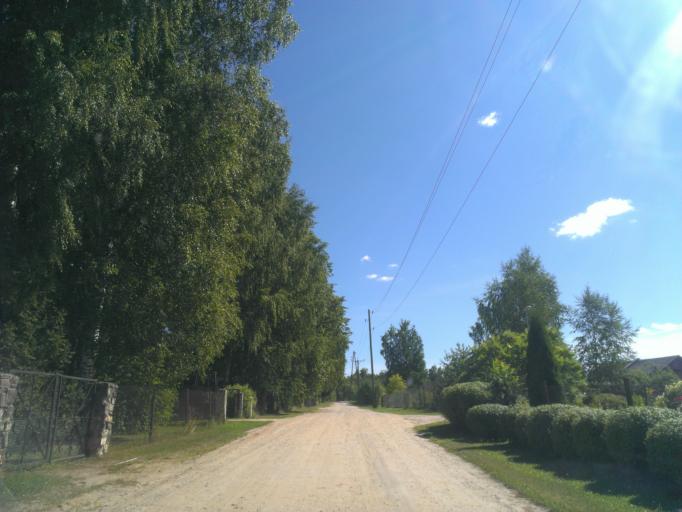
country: LV
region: Malpils
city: Malpils
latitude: 57.0112
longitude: 24.9662
